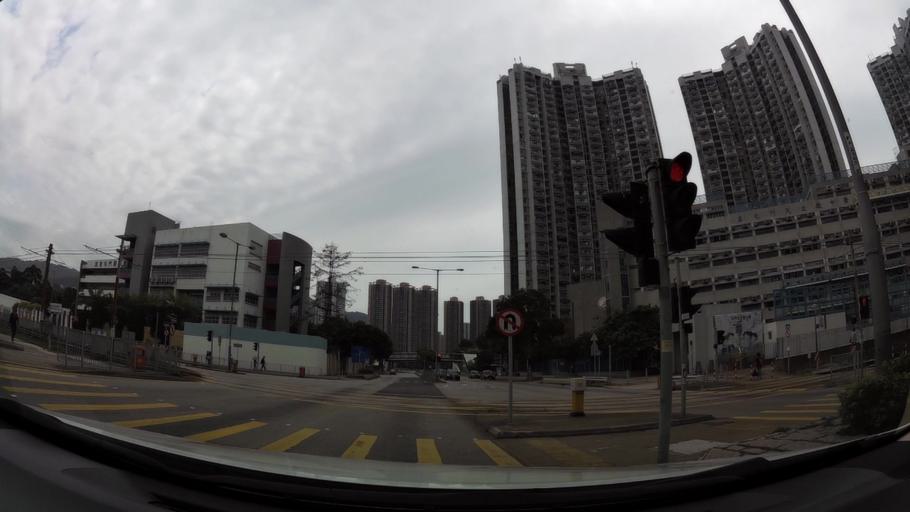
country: HK
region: Tuen Mun
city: Tuen Mun
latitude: 22.4072
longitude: 113.9713
